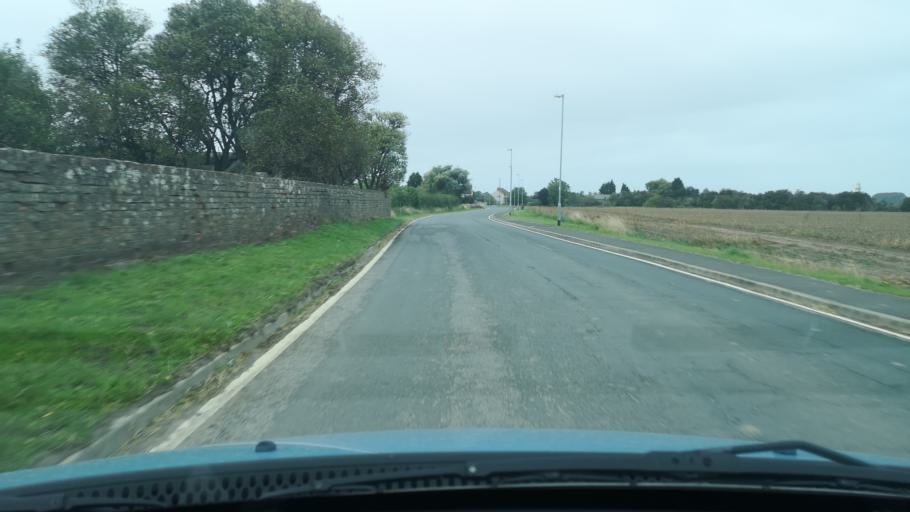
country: GB
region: England
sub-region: East Riding of Yorkshire
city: Laxton
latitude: 53.6979
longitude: -0.7509
